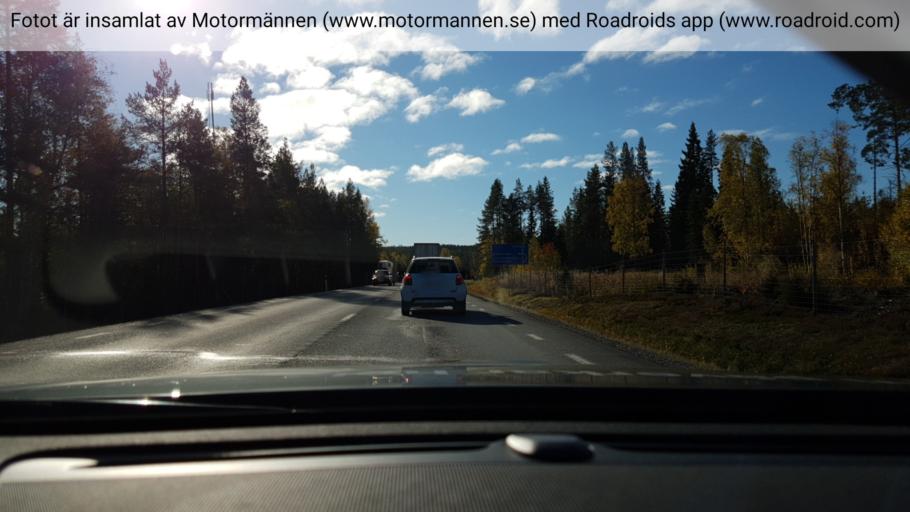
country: SE
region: Vaesterbotten
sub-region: Skelleftea Kommun
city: Burea
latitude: 64.4696
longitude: 21.2927
